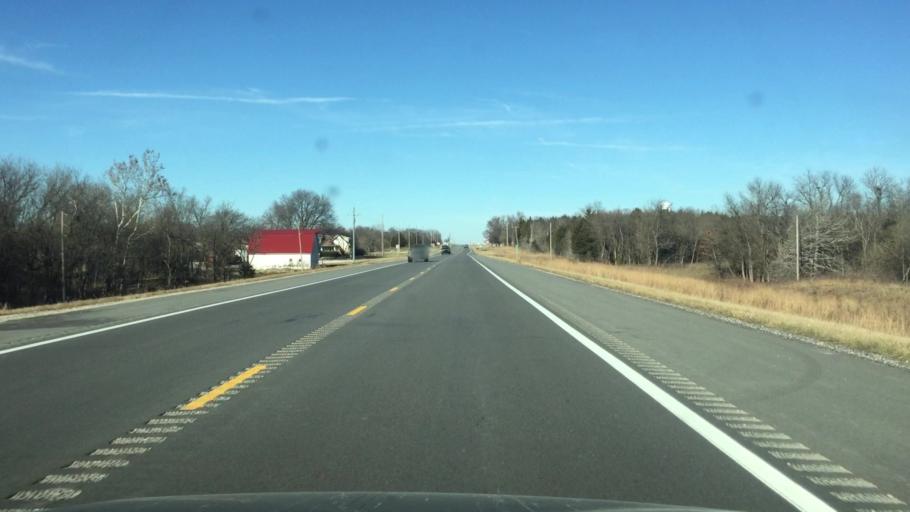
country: US
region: Kansas
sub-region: Franklin County
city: Ottawa
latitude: 38.4810
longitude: -95.2674
